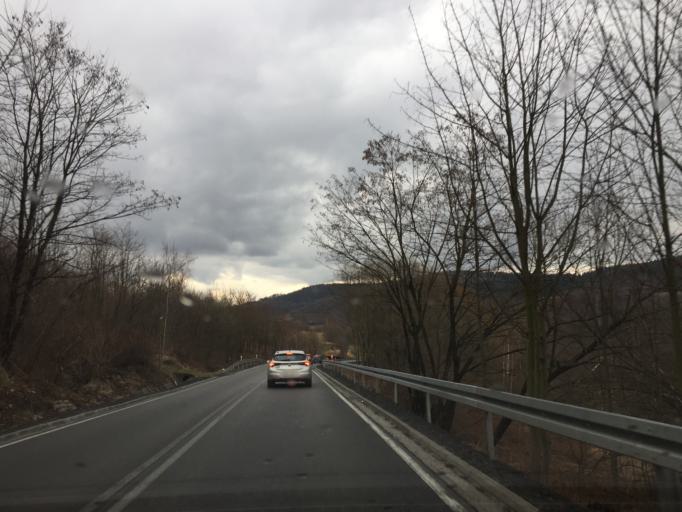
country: PL
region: Lesser Poland Voivodeship
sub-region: Powiat suski
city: Palcza
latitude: 49.8082
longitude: 19.7617
